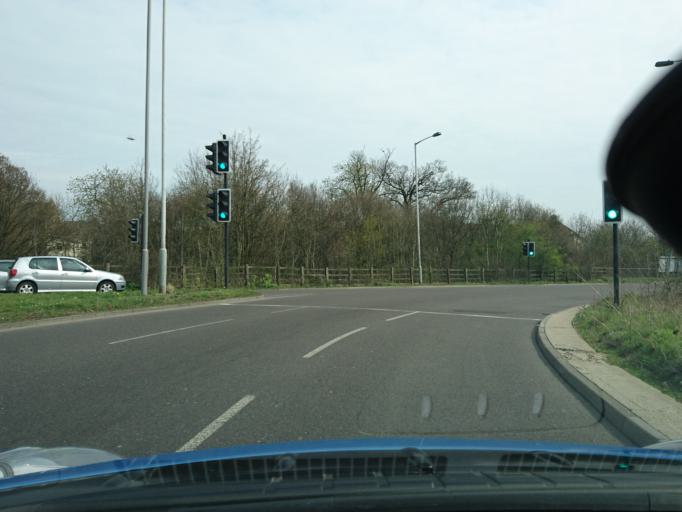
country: GB
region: England
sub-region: Greater London
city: Woodford Green
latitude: 51.5964
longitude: 0.0113
